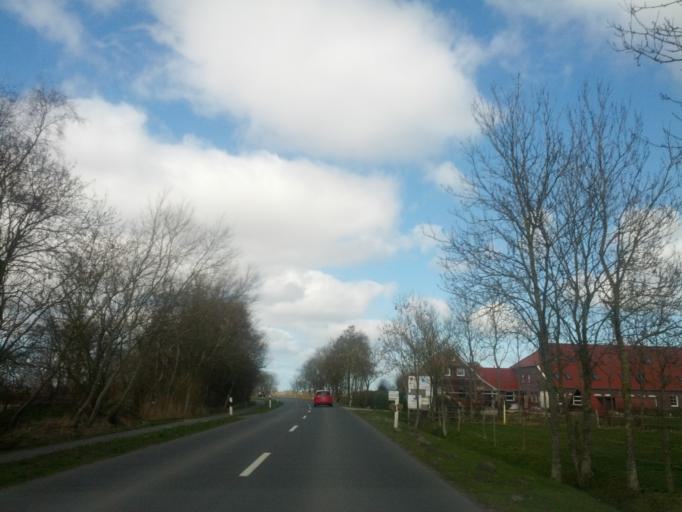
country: DE
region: Lower Saxony
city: Esens
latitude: 53.6615
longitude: 7.6028
